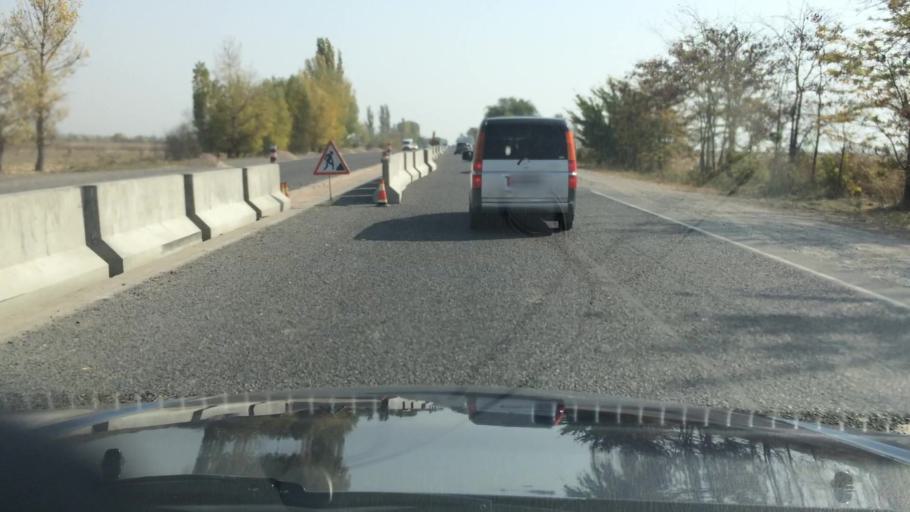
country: KG
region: Chuy
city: Kant
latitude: 42.9582
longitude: 74.9270
